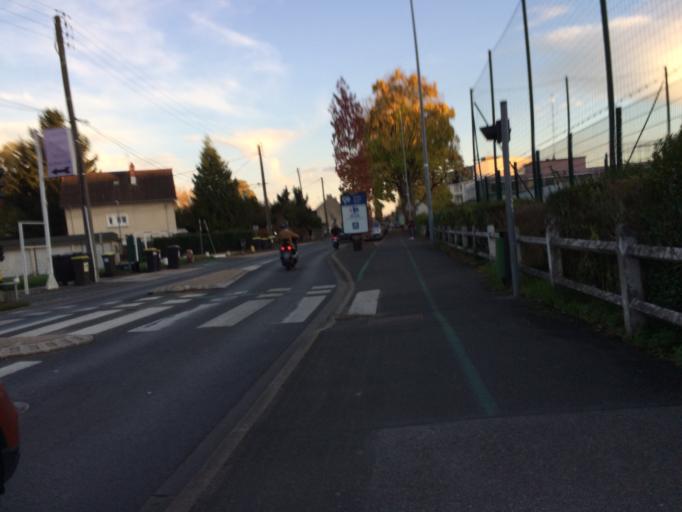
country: FR
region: Ile-de-France
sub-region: Departement de l'Essonne
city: Sainte-Genevieve-des-Bois
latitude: 48.6321
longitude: 2.3365
